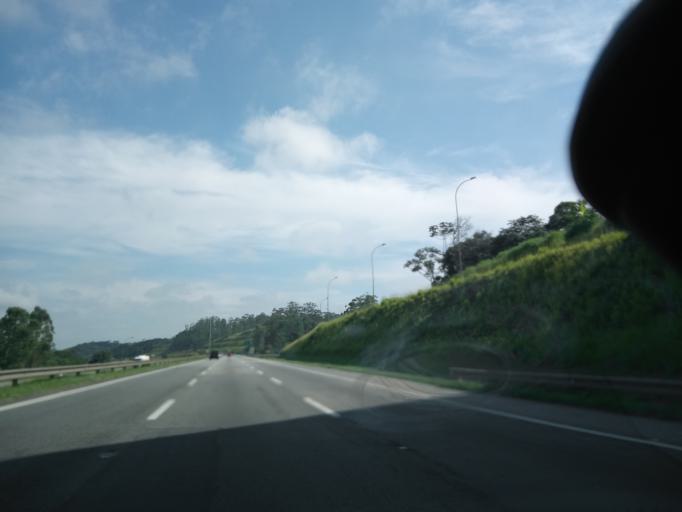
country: BR
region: Sao Paulo
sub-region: Itapecerica Da Serra
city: Itapecerica da Serra
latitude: -23.6915
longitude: -46.8187
